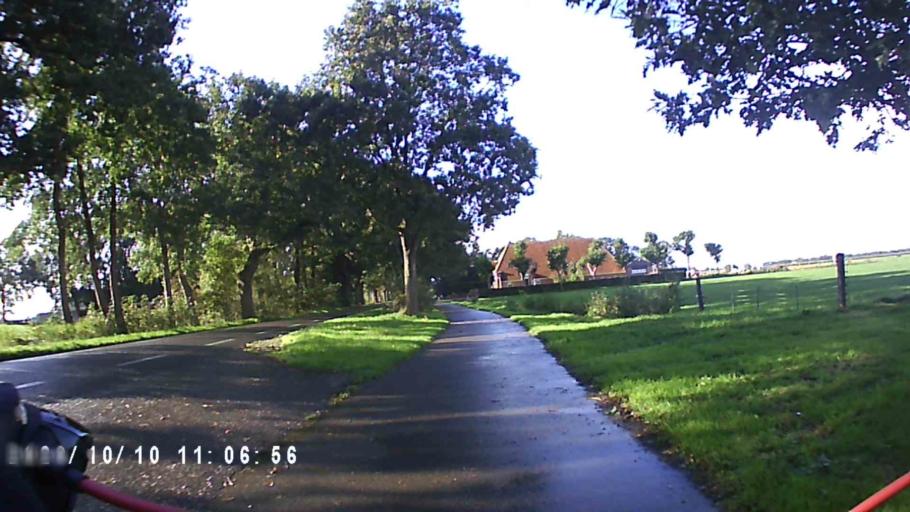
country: NL
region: Friesland
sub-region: Gemeente Smallingerland
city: Drachtstercompagnie
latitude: 53.1248
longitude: 6.2158
